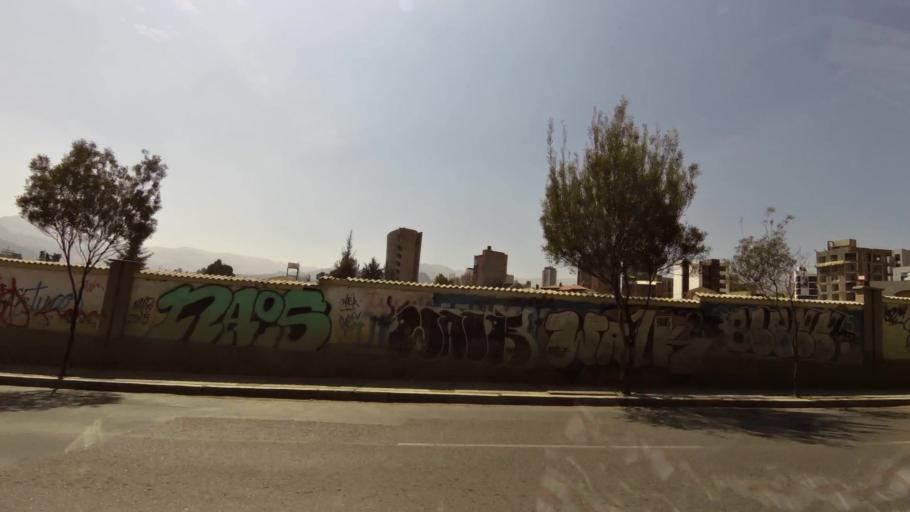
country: BO
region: La Paz
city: La Paz
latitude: -16.5456
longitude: -68.0816
